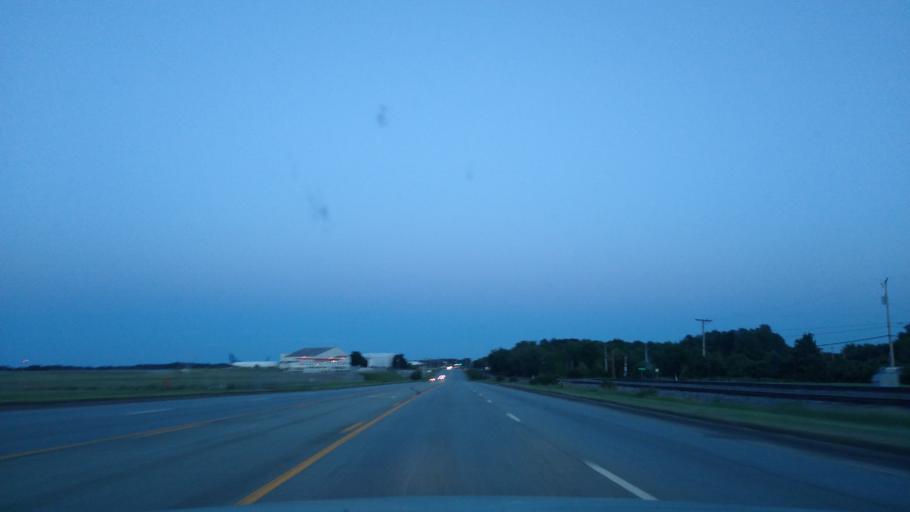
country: US
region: North Carolina
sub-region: Guilford County
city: Oak Ridge
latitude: 36.0907
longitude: -79.9484
